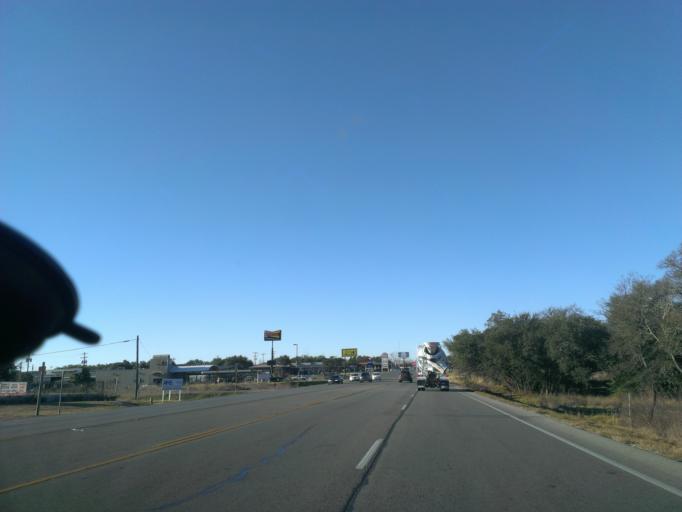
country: US
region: Texas
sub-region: Travis County
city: Bee Cave
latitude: 30.2141
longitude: -97.9661
